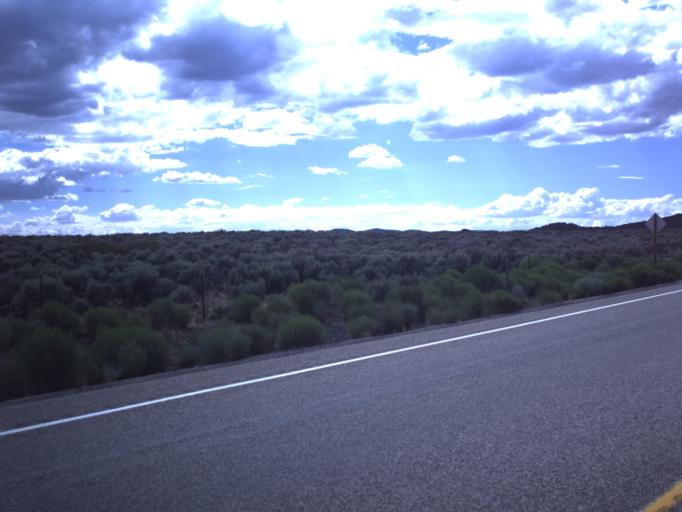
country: US
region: Utah
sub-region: Beaver County
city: Beaver
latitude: 38.0645
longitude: -112.5946
